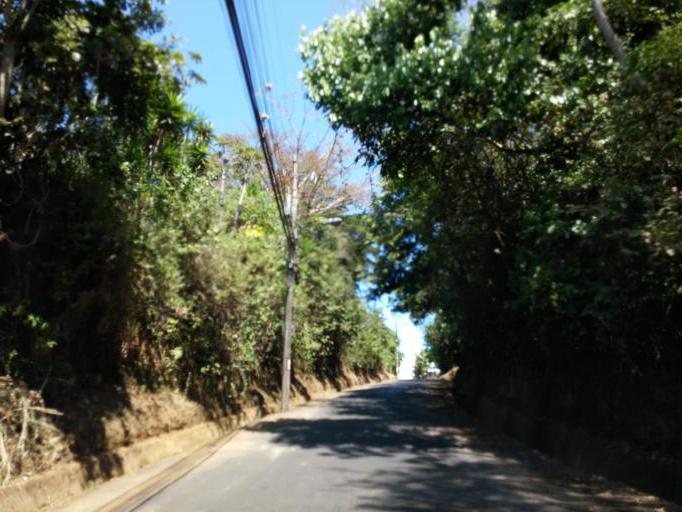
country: CR
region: Heredia
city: Santo Domingo
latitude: 10.0482
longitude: -84.1411
